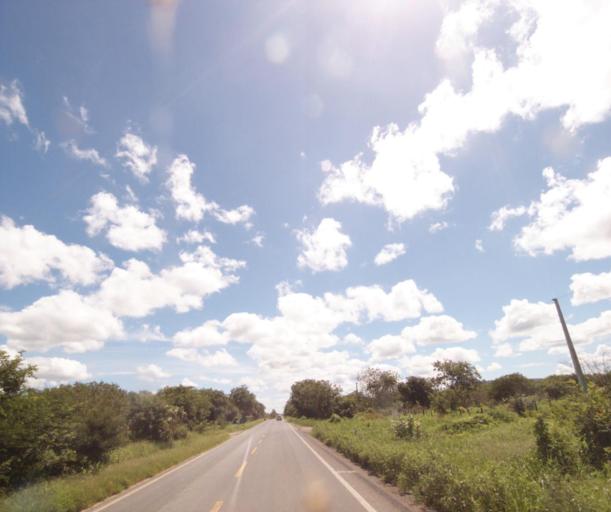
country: BR
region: Bahia
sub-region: Sao Felix Do Coribe
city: Santa Maria da Vitoria
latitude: -13.4053
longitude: -44.1549
